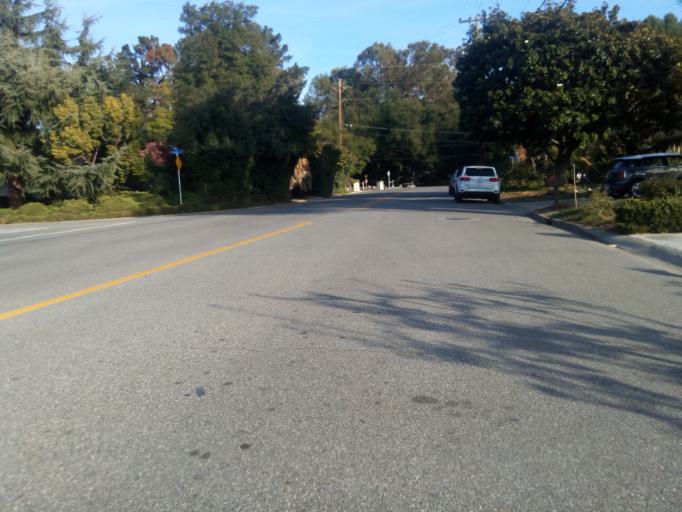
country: US
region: California
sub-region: Santa Clara County
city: Mountain View
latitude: 37.3714
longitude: -122.0692
